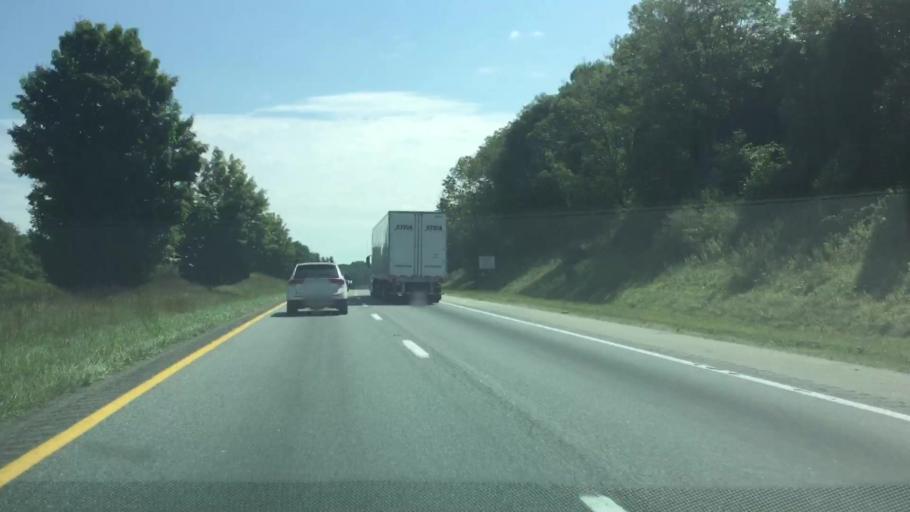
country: US
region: Virginia
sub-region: City of Radford
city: Radford
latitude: 37.0988
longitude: -80.5426
